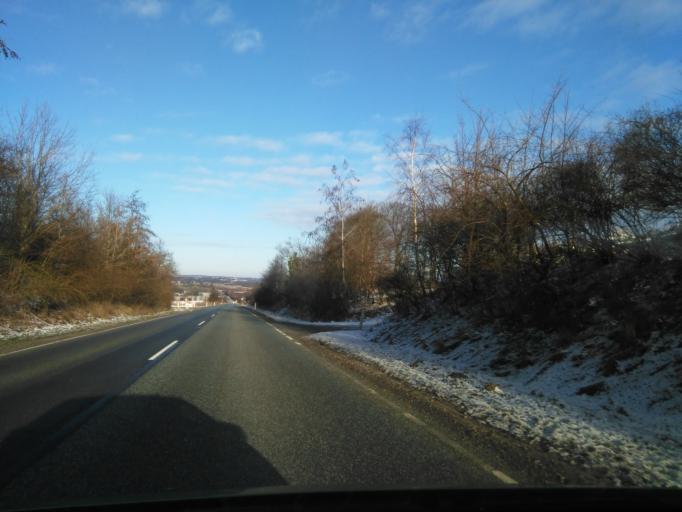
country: DK
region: Central Jutland
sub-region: Arhus Kommune
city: Framlev
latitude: 56.1185
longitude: 9.9881
